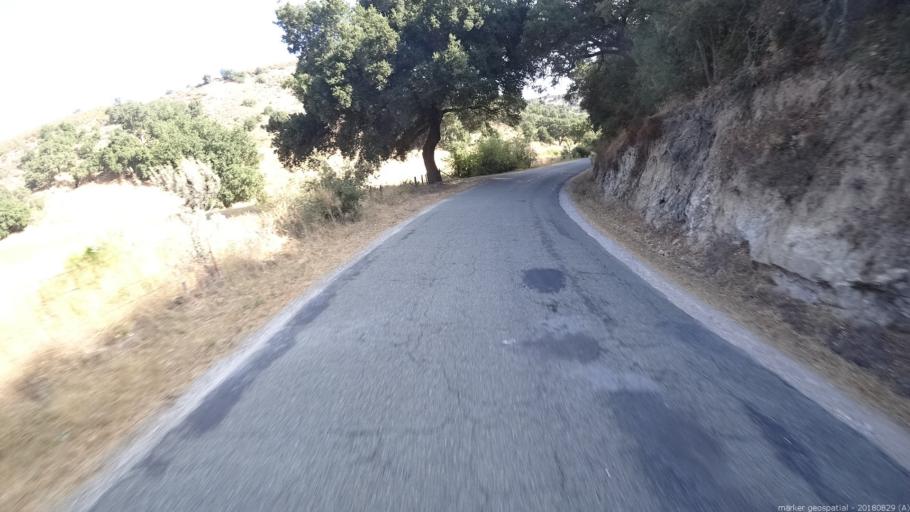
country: US
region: California
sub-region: Monterey County
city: King City
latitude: 36.0400
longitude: -121.0796
